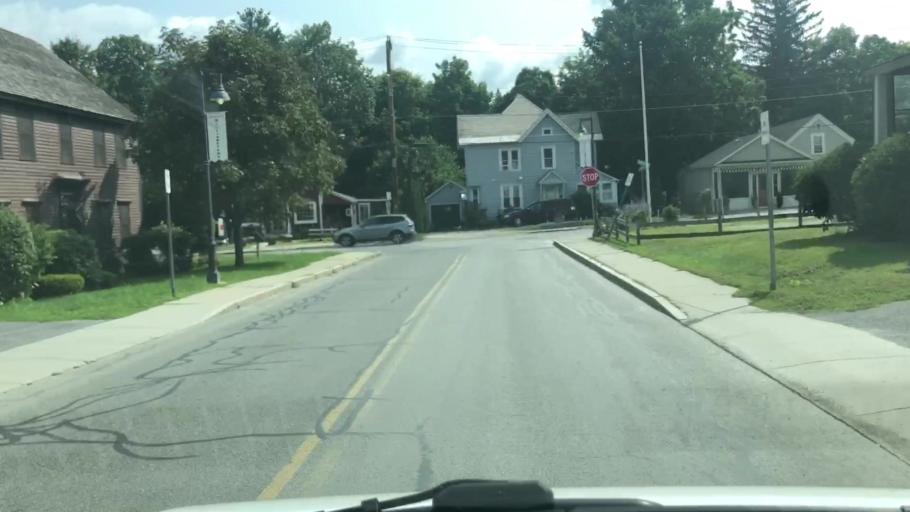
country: US
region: Massachusetts
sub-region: Berkshire County
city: Williamstown
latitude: 42.7084
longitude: -73.2012
